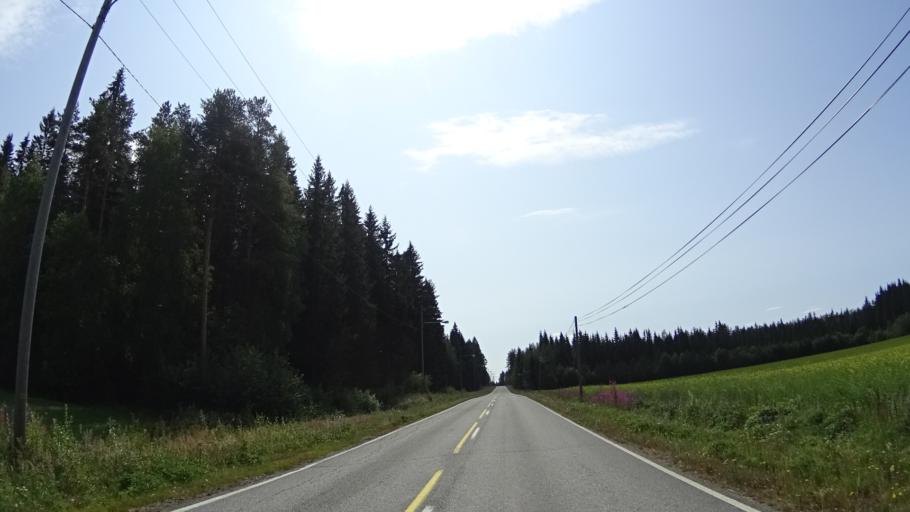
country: FI
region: Pirkanmaa
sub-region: Ylae-Pirkanmaa
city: Maenttae
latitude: 61.8879
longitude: 24.7918
